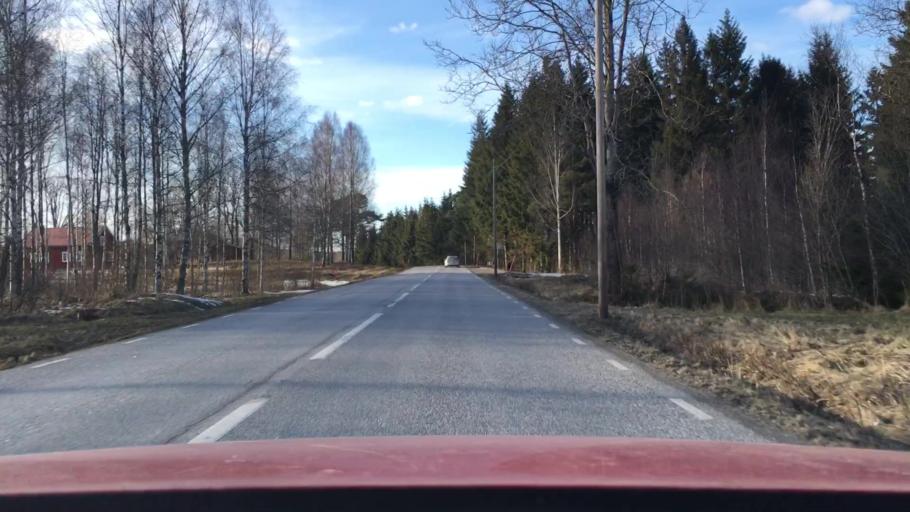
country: SE
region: Vaestra Goetaland
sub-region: Tanums Kommun
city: Tanumshede
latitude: 58.8100
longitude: 11.5506
